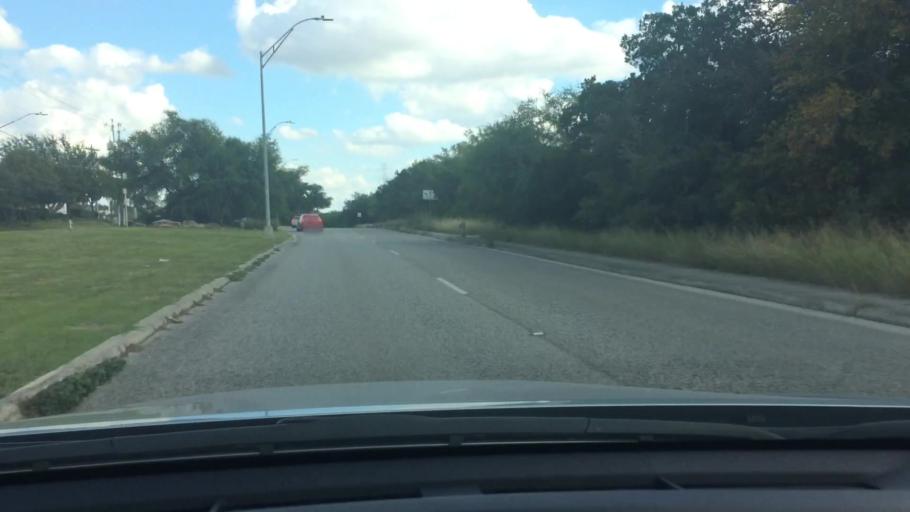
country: US
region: Texas
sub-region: Bexar County
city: Hollywood Park
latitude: 29.6357
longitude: -98.4534
